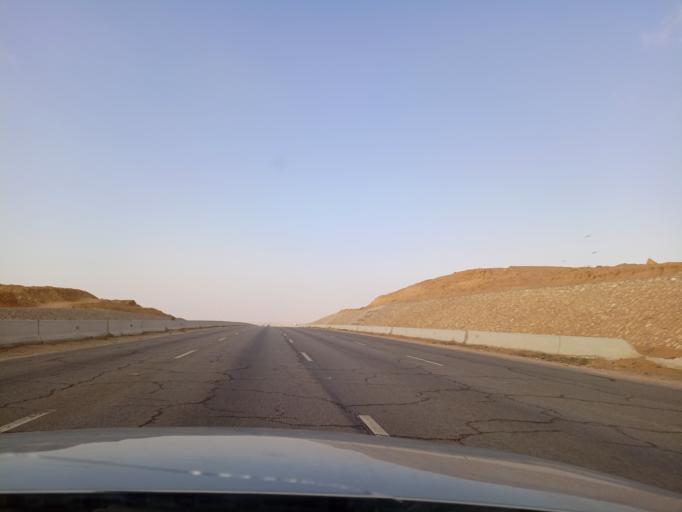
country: EG
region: Al Jizah
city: Al `Ayyat
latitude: 29.6651
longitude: 31.1747
